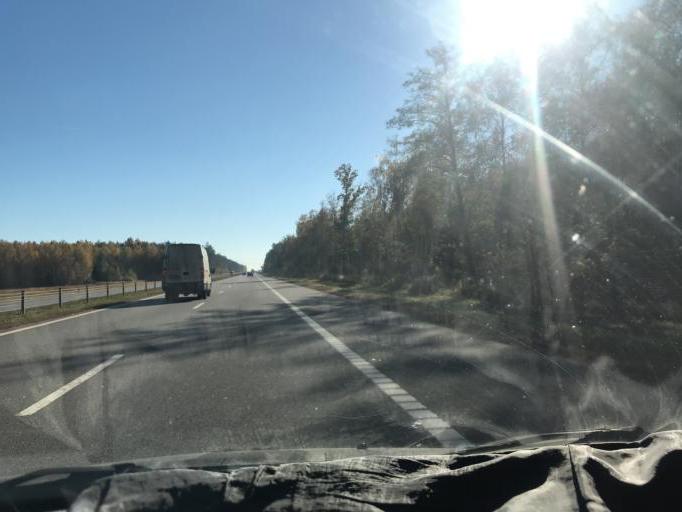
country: BY
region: Mogilev
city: Yalizava
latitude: 53.2654
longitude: 28.8854
